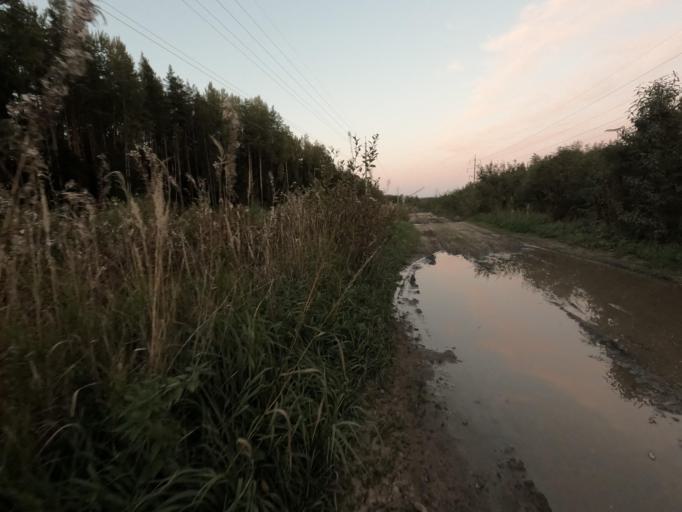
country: RU
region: Leningrad
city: Otradnoye
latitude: 59.7721
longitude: 30.8599
